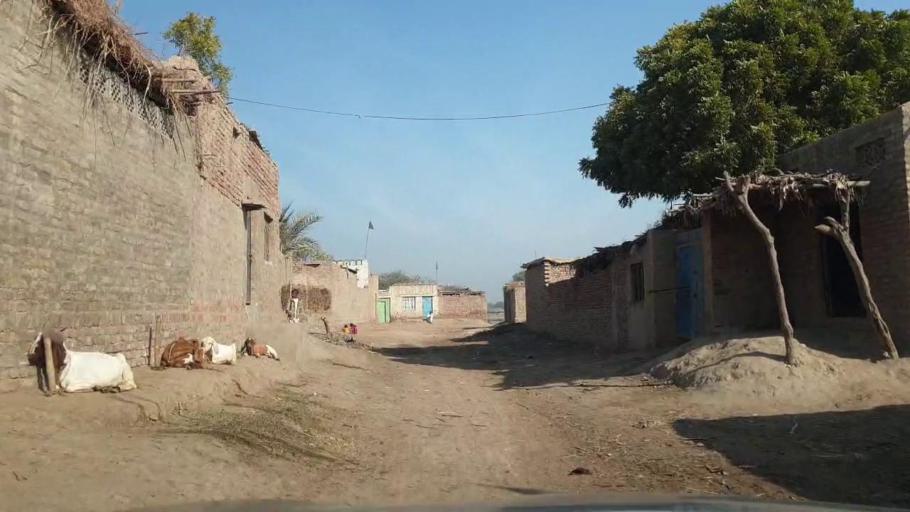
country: PK
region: Sindh
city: Tando Allahyar
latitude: 25.5929
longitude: 68.7233
